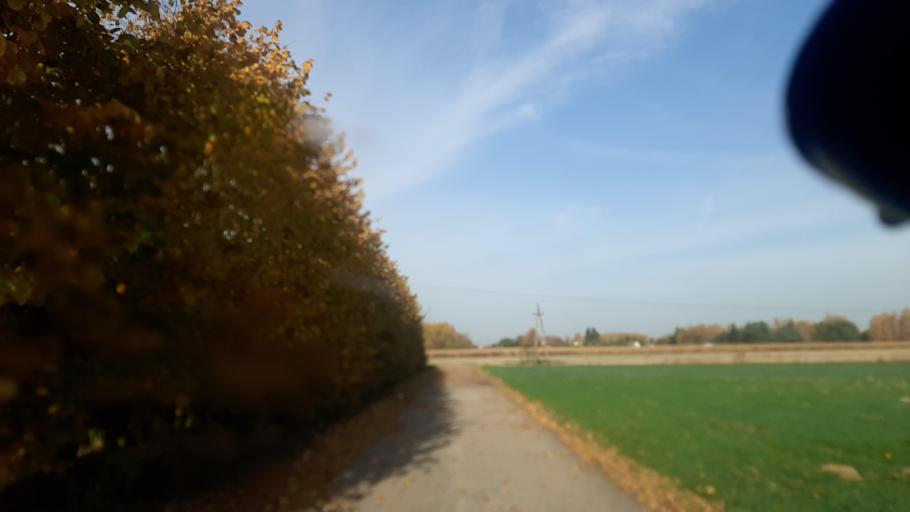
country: PL
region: Lublin Voivodeship
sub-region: Powiat lubelski
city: Lublin
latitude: 51.3305
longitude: 22.5440
